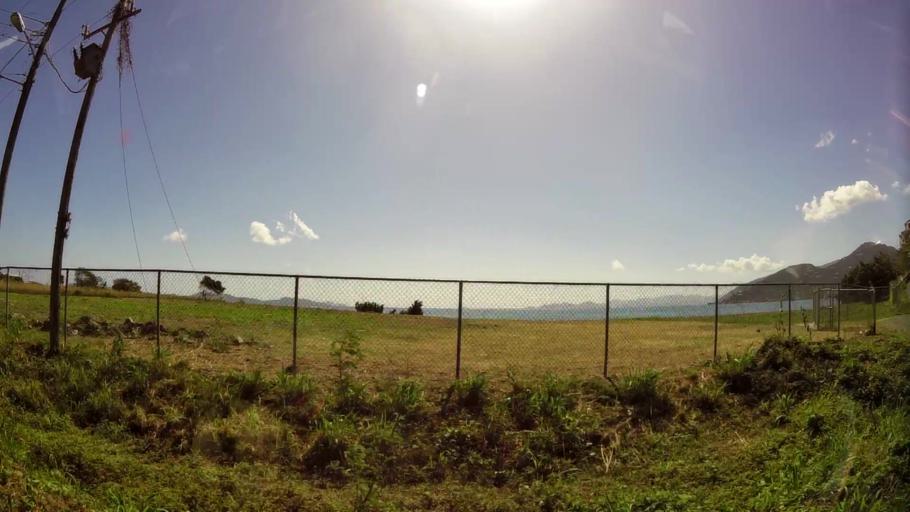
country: VG
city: Tortola
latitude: 18.4167
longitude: -64.5968
